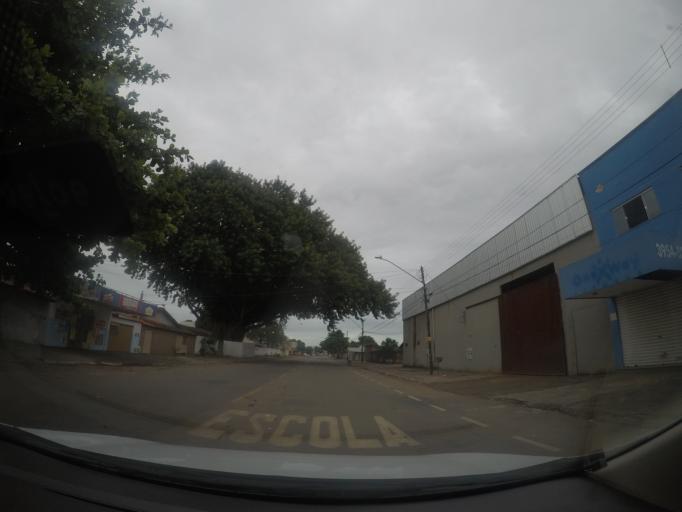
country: BR
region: Goias
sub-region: Goiania
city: Goiania
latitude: -16.6859
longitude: -49.3338
